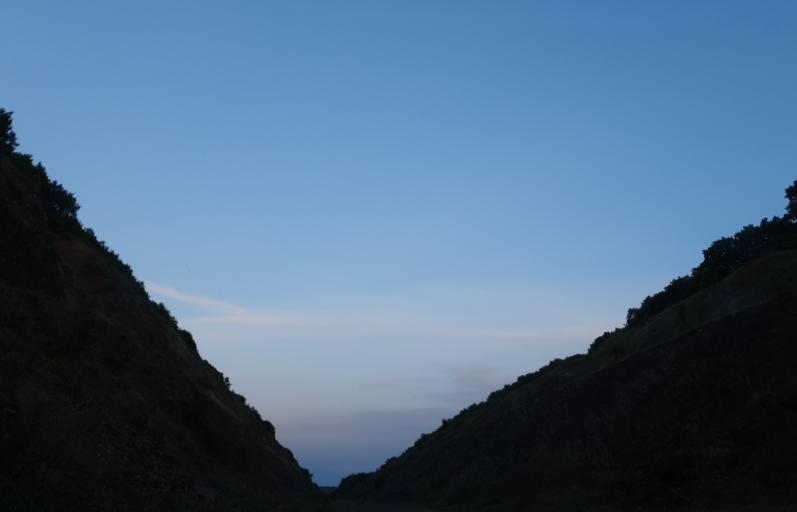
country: TR
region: Kirklareli
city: Salmydessus
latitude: 41.6865
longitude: 28.0825
